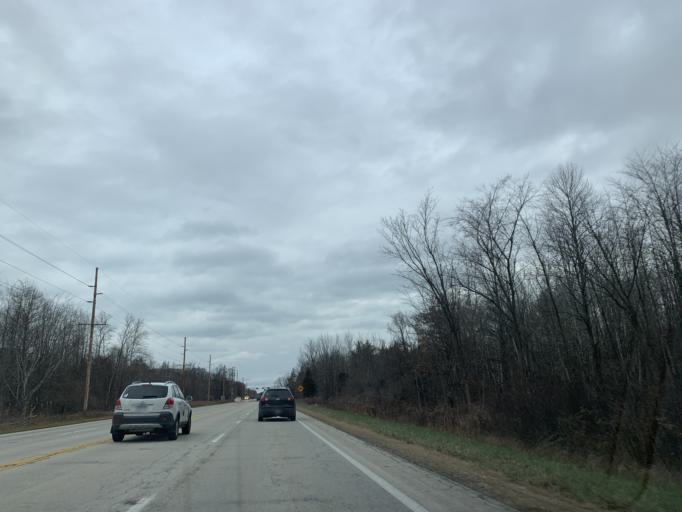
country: US
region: Indiana
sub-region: LaPorte County
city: Long Beach
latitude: 41.7274
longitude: -86.8261
